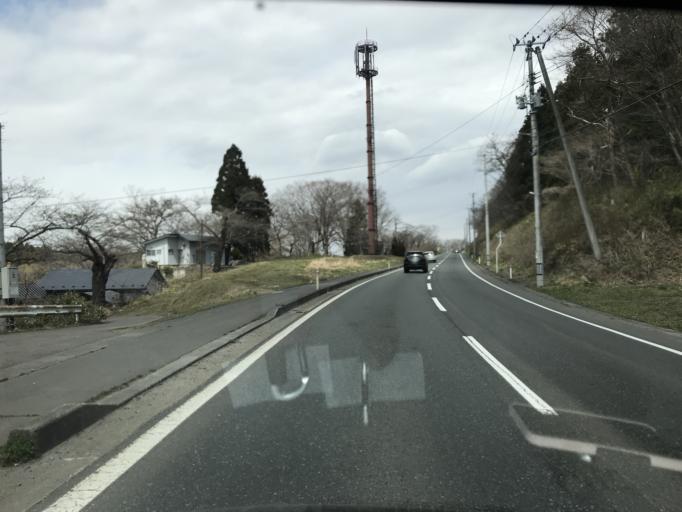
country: JP
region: Iwate
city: Kitakami
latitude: 39.2607
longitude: 141.1230
